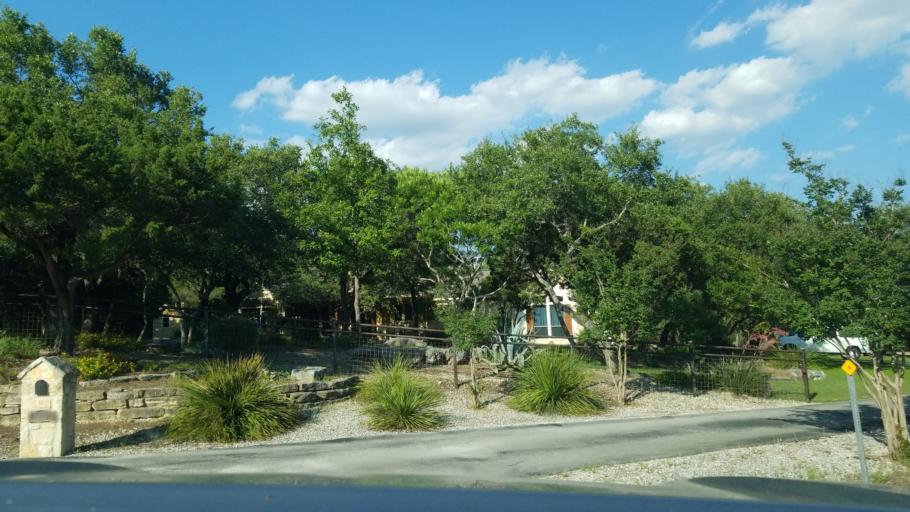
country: US
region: Texas
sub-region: Comal County
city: Bulverde
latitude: 29.7892
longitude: -98.4250
